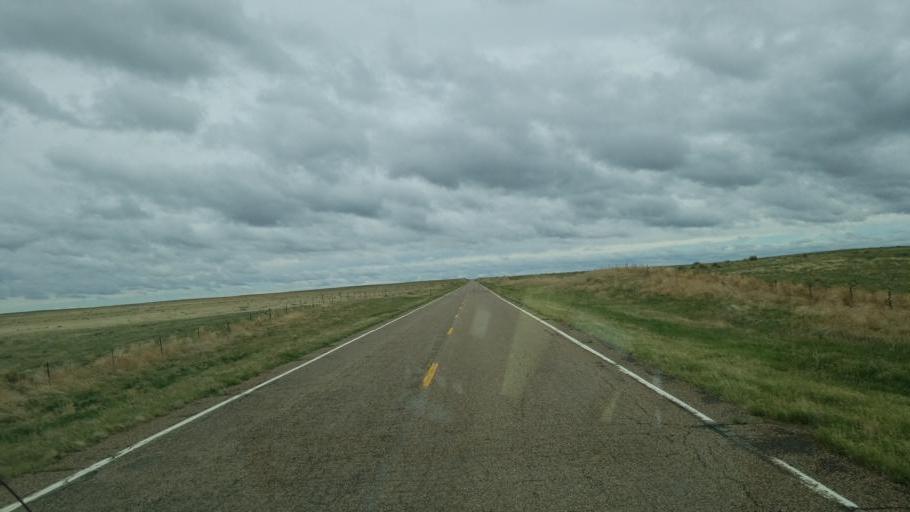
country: US
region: Colorado
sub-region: Lincoln County
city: Hugo
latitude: 38.8507
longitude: -103.5649
